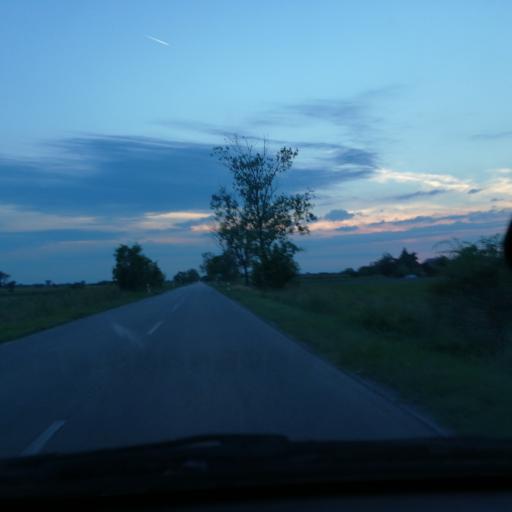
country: HU
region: Bacs-Kiskun
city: Kalocsa
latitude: 46.5091
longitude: 19.0807
